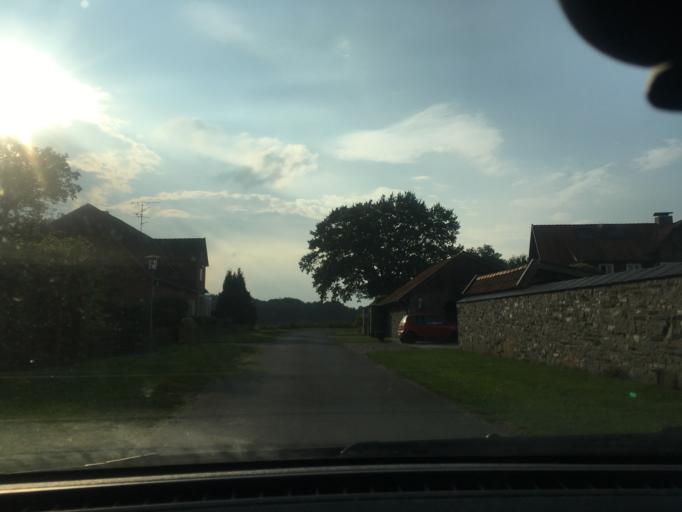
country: DE
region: Lower Saxony
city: Reinstorf
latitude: 53.2027
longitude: 10.5787
